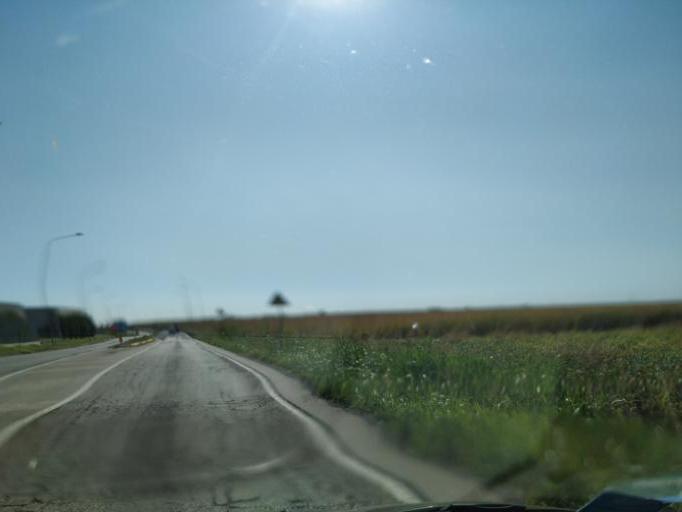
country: IT
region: Emilia-Romagna
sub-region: Provincia di Bologna
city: Decima
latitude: 44.6986
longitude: 11.2291
